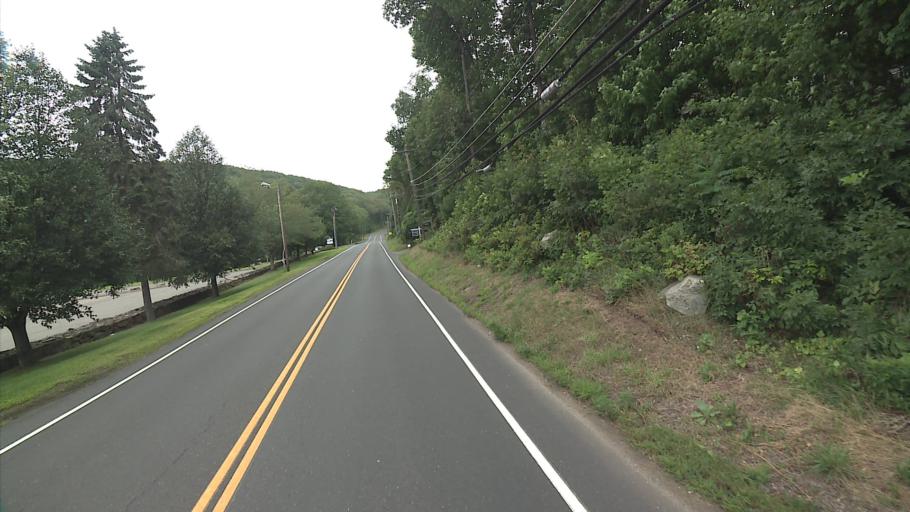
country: US
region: Connecticut
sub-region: Tolland County
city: Tolland
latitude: 41.8750
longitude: -72.3751
